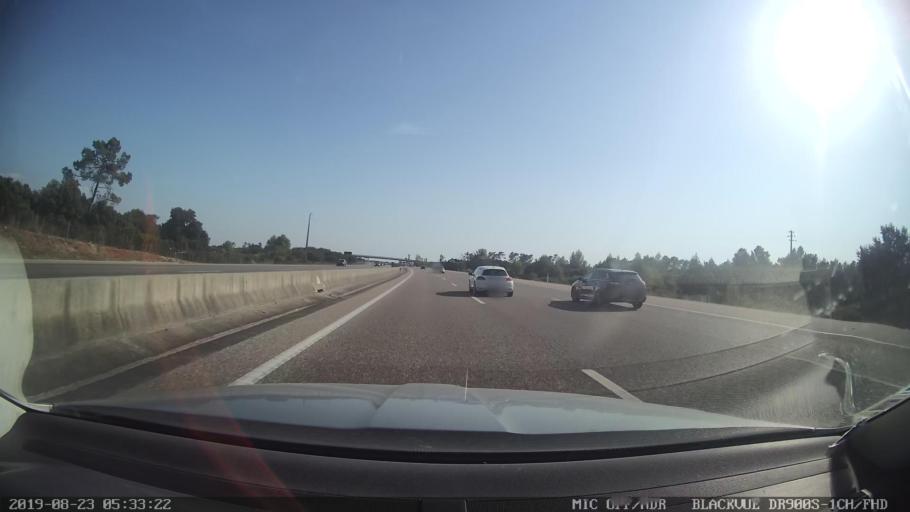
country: PT
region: Santarem
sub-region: Alcanena
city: Alcanena
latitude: 39.4262
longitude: -8.6312
